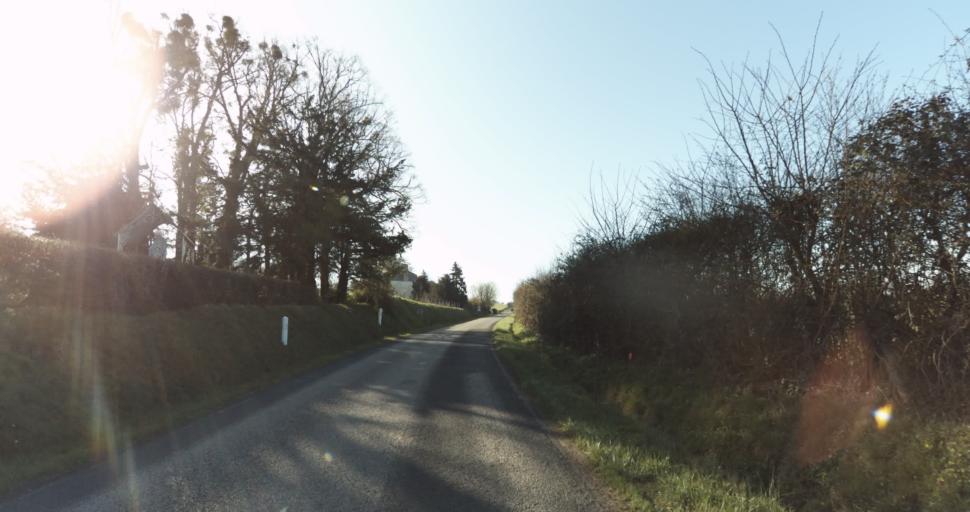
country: FR
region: Lower Normandy
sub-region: Departement du Calvados
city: Saint-Pierre-sur-Dives
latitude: 49.0155
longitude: -0.0216
